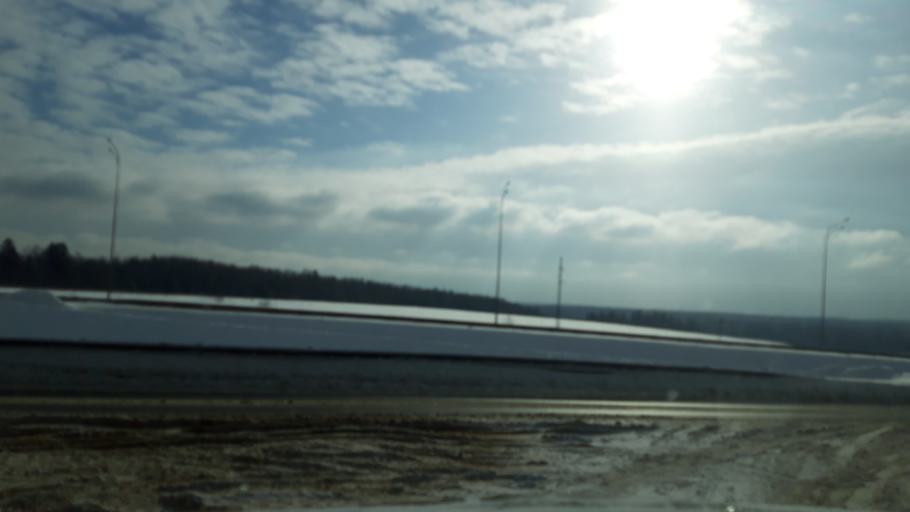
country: RU
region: Moskovskaya
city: Yermolino
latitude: 56.1349
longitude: 37.3777
